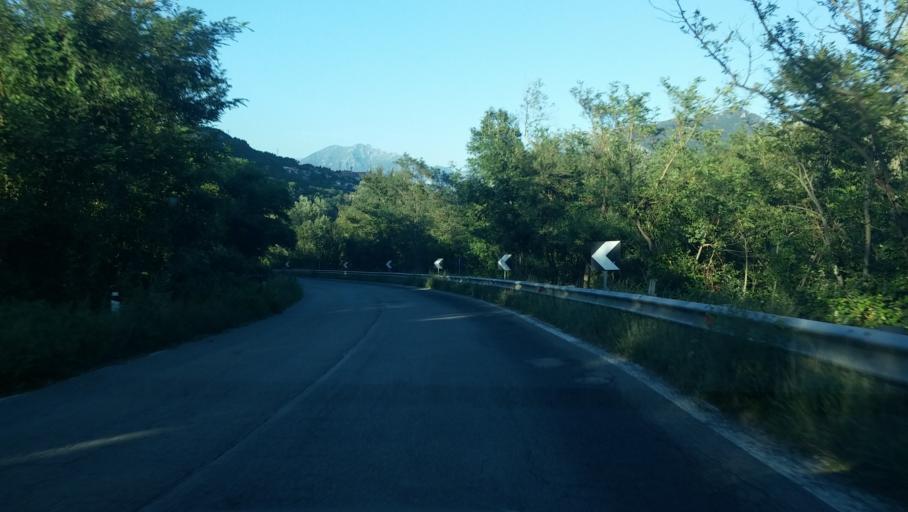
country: IT
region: Lombardy
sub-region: Provincia di Lecco
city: Suello
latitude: 45.8201
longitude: 9.3235
